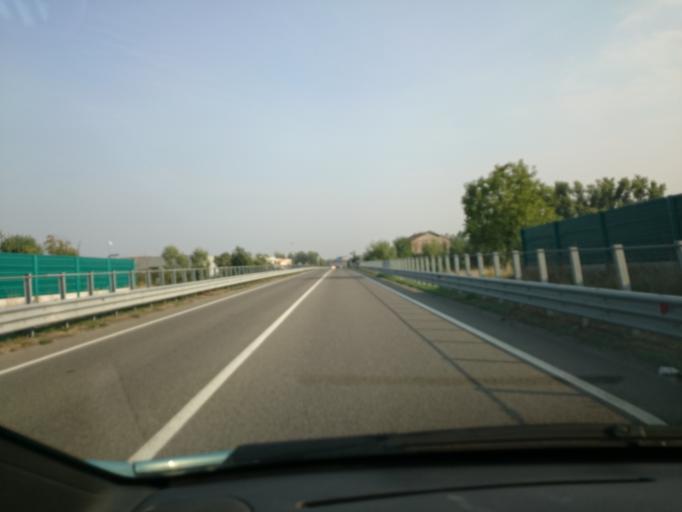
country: IT
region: Emilia-Romagna
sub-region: Provincia di Reggio Emilia
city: Casalgrande
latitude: 44.5891
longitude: 10.7192
